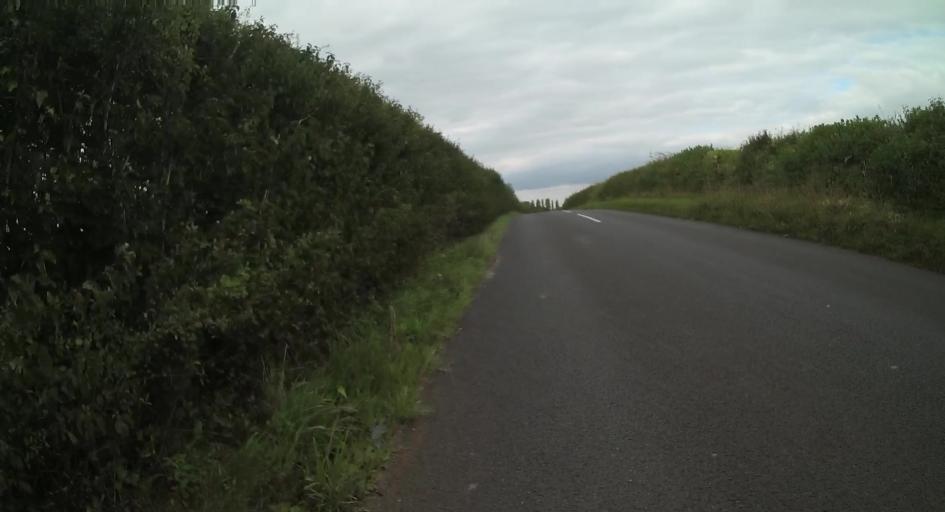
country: GB
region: England
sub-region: Isle of Wight
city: Yarmouth
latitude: 50.6961
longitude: -1.4826
